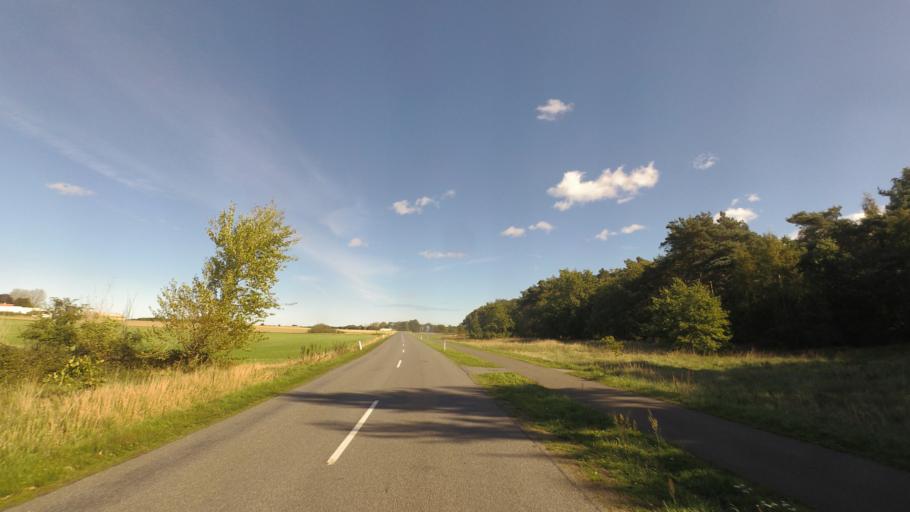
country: DK
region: Capital Region
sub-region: Bornholm Kommune
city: Nexo
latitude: 55.0025
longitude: 15.0791
